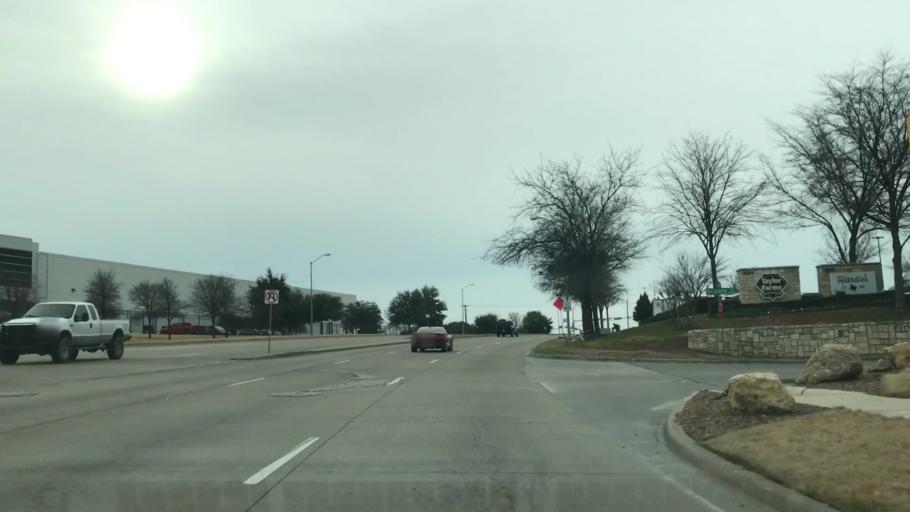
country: US
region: Texas
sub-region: Dallas County
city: Cockrell Hill
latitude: 32.7519
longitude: -96.8919
